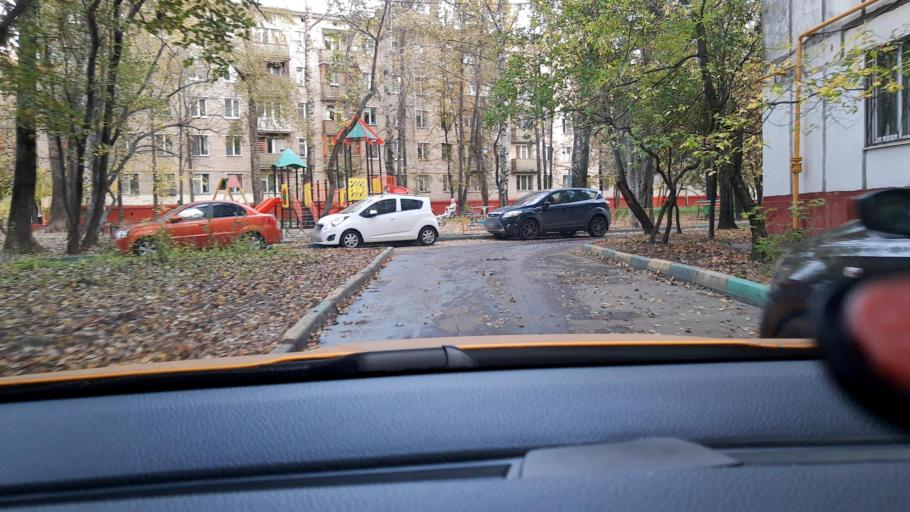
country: RU
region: Moscow
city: Businovo
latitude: 55.8780
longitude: 37.5176
